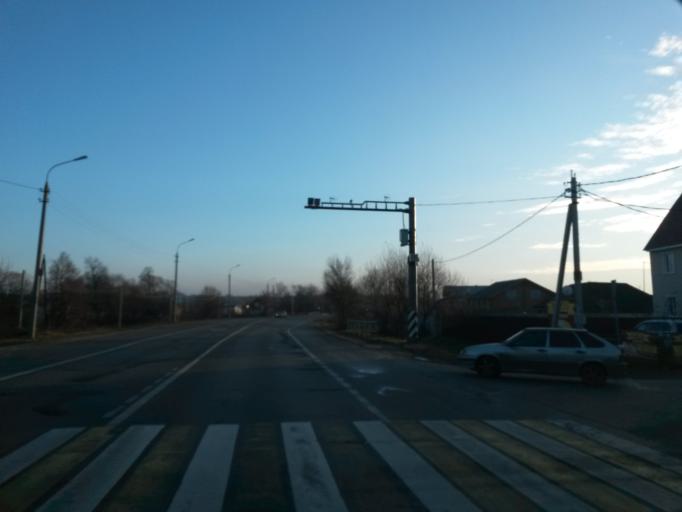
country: RU
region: Moskovskaya
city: Stolbovaya
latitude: 55.2699
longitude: 37.5112
